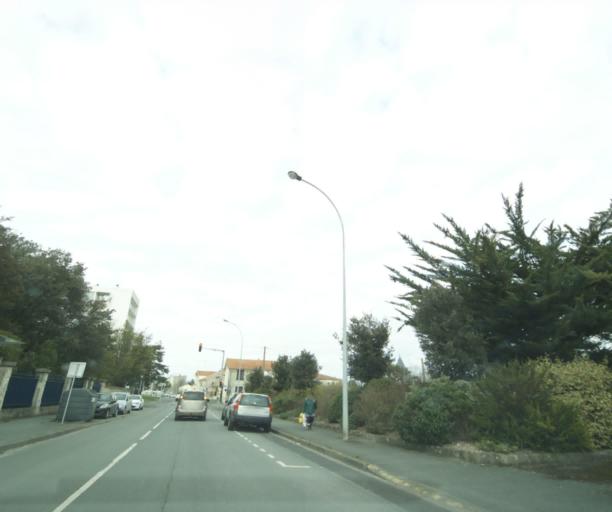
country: FR
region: Poitou-Charentes
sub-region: Departement de la Charente-Maritime
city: La Rochelle
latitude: 46.1662
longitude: -1.1642
